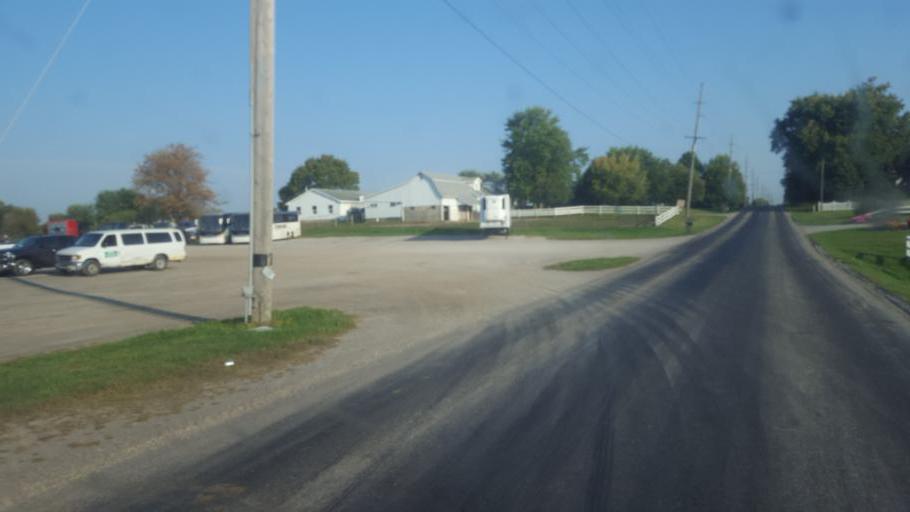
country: US
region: Indiana
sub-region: LaGrange County
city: Topeka
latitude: 41.6556
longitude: -85.5561
